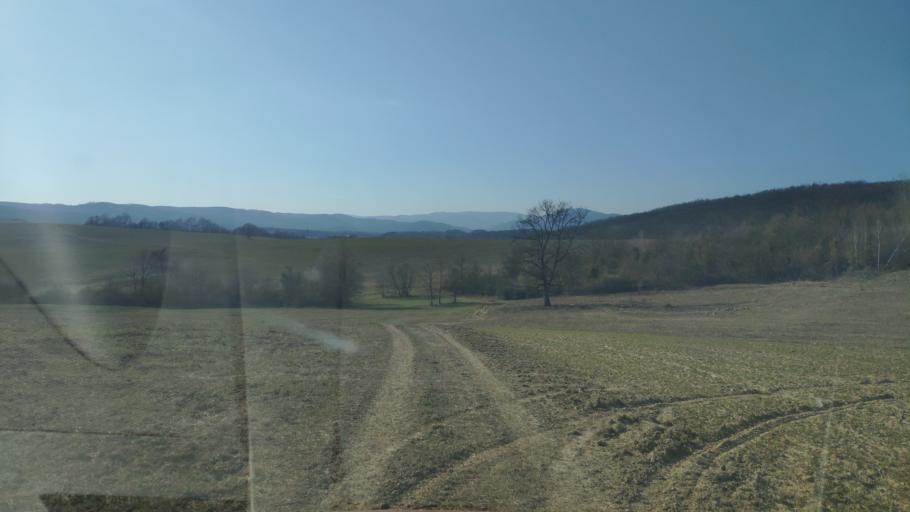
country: SK
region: Banskobystricky
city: Revuca
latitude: 48.5521
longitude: 20.2650
